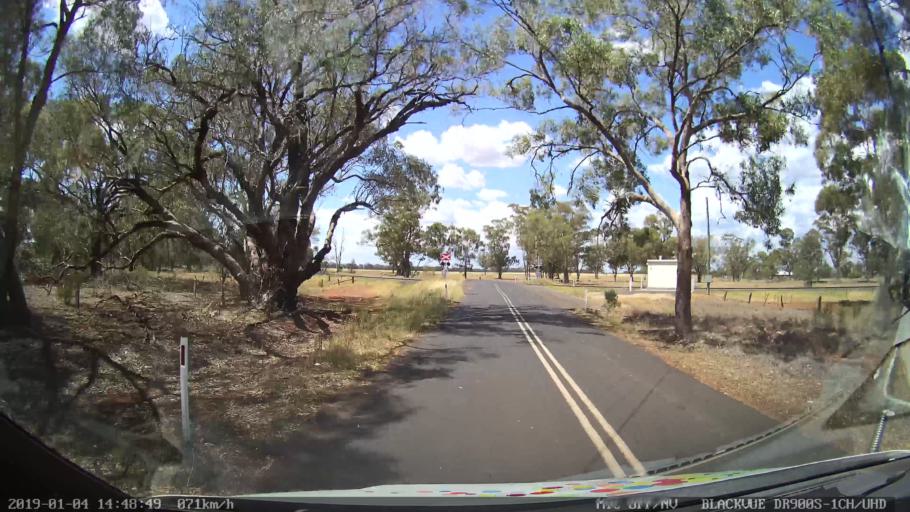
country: AU
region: New South Wales
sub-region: Dubbo Municipality
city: Dubbo
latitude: -32.0553
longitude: 148.6647
